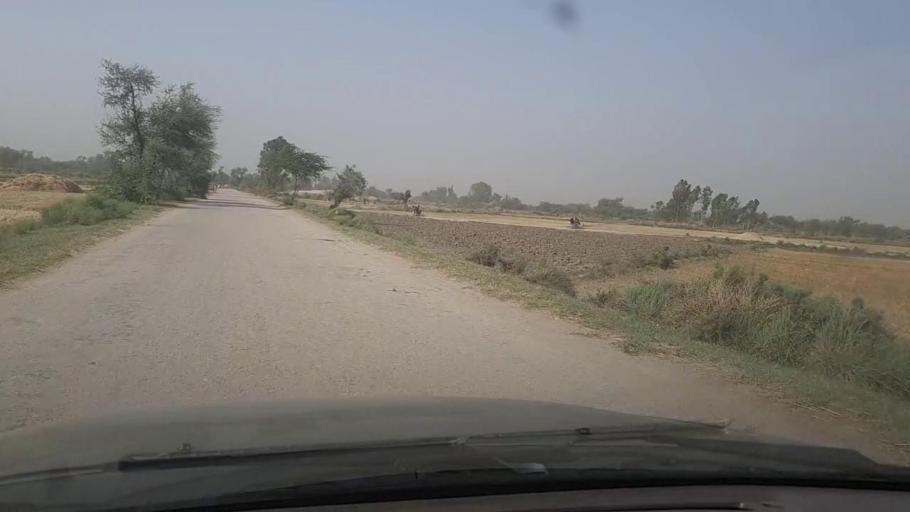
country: PK
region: Sindh
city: Shikarpur
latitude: 27.9173
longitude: 68.6091
